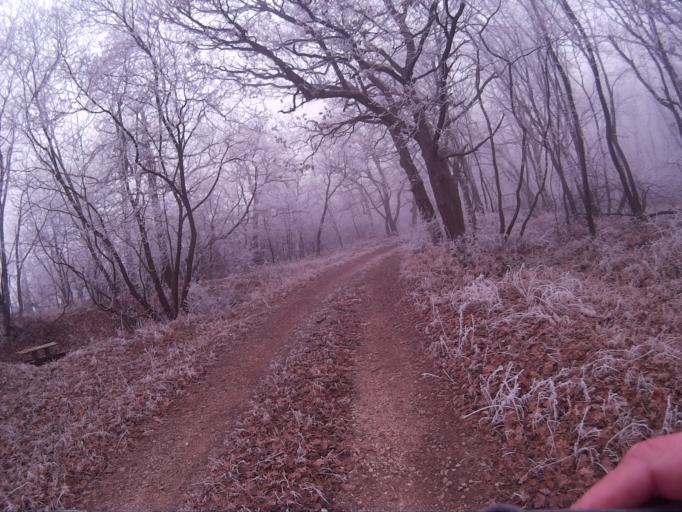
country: HU
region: Komarom-Esztergom
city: Oroszlany
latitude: 47.3933
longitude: 18.3303
